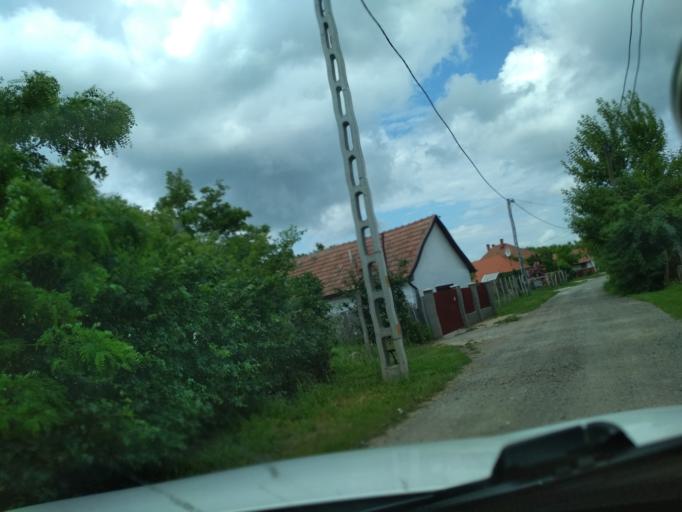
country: HU
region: Jasz-Nagykun-Szolnok
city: Tiszafured
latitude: 47.6058
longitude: 20.7479
